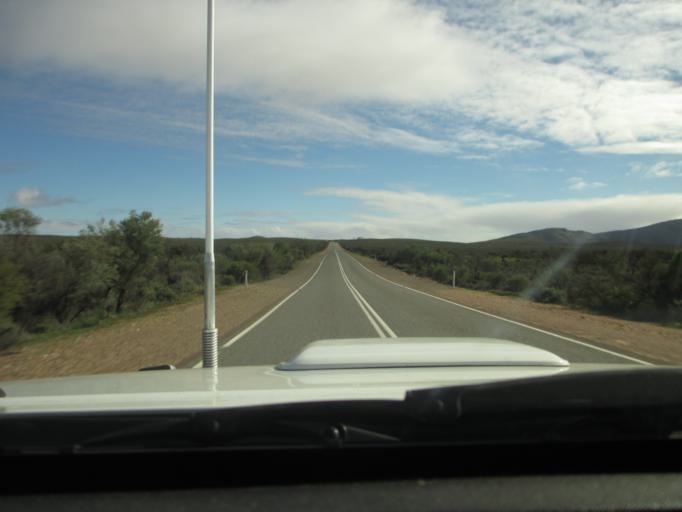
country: AU
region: South Australia
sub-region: Flinders Ranges
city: Quorn
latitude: -31.8207
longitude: 138.3782
